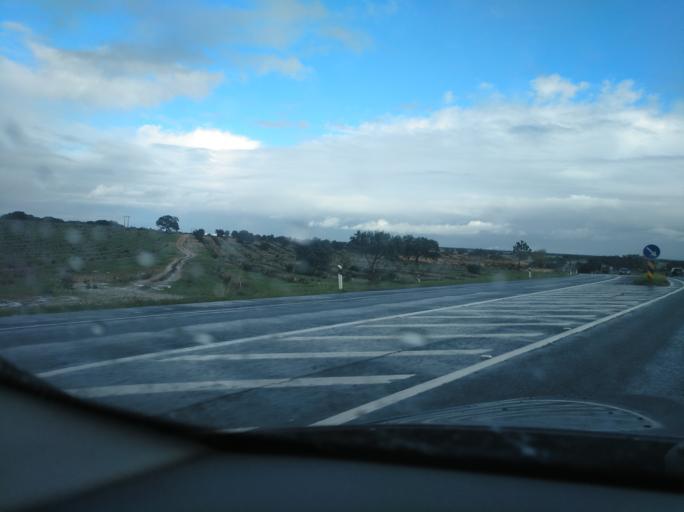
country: PT
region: Setubal
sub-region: Grandola
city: Grandola
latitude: 38.0138
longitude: -8.3936
